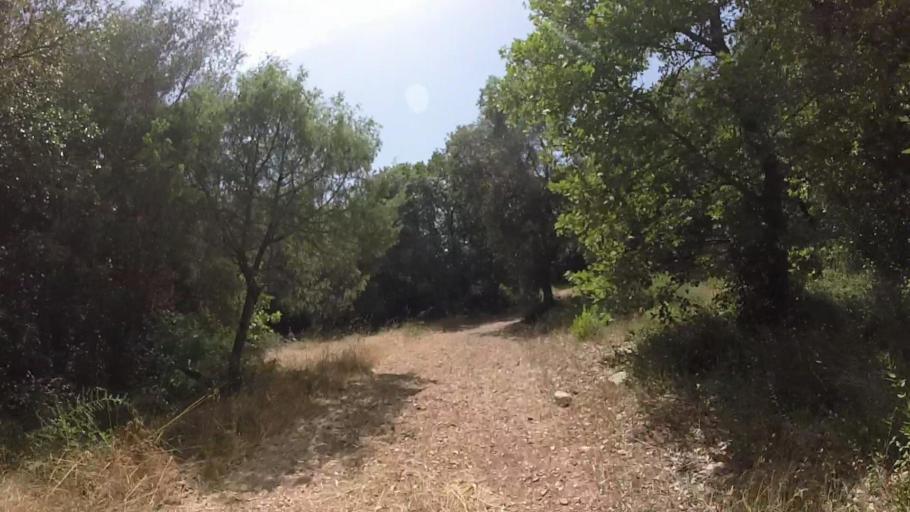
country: FR
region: Provence-Alpes-Cote d'Azur
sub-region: Departement des Alpes-Maritimes
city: Mougins
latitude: 43.6159
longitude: 7.0304
